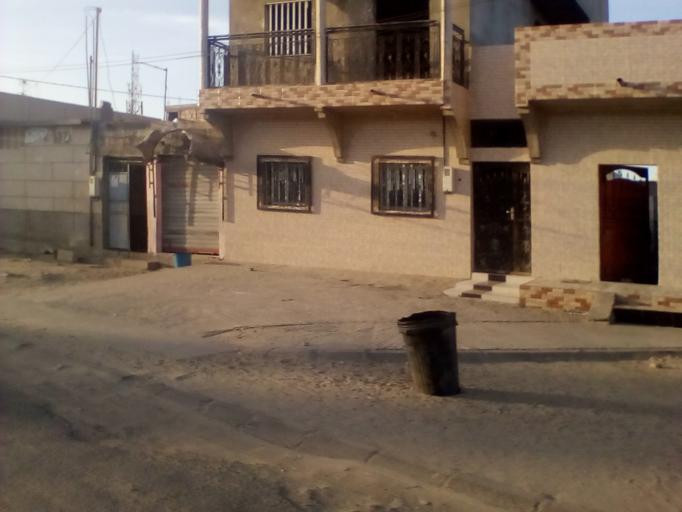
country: SN
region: Saint-Louis
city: Saint-Louis
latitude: 16.0184
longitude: -16.4917
